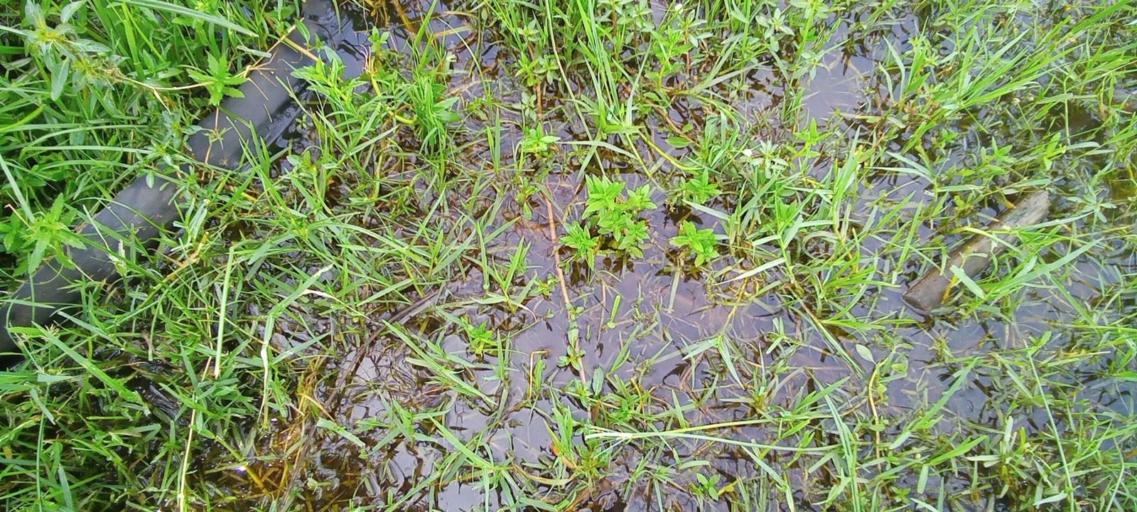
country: KE
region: Homa Bay
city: Homa Bay
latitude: -0.4625
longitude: 34.1845
